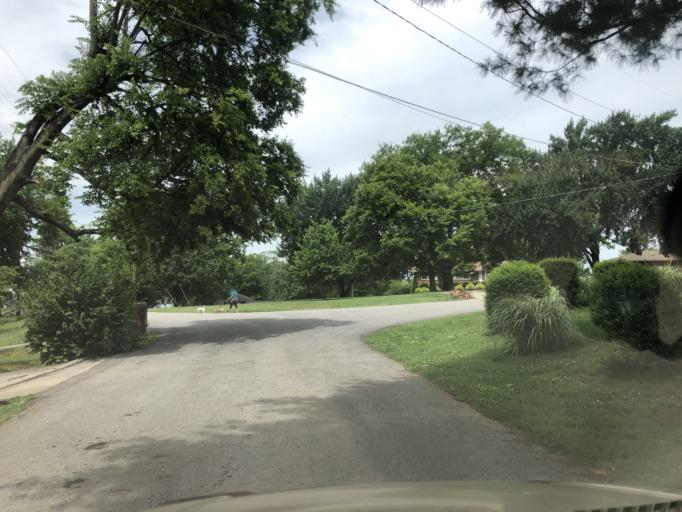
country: US
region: Tennessee
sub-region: Davidson County
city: Lakewood
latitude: 36.2530
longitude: -86.6195
